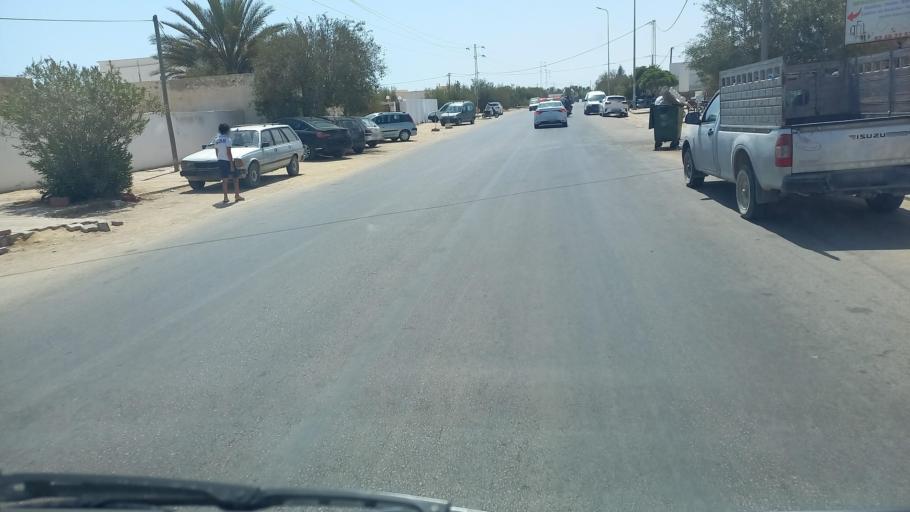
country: TN
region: Madanin
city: Houmt Souk
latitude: 33.7983
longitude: 10.8847
